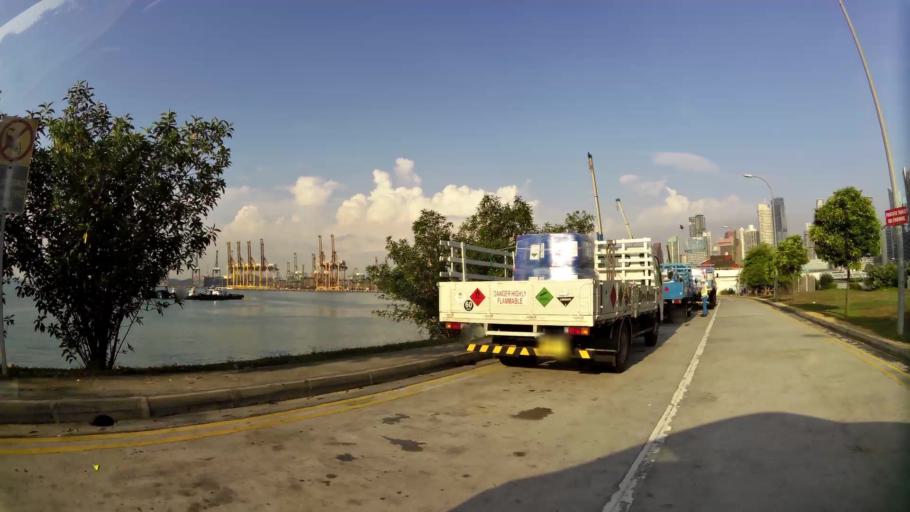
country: SG
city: Singapore
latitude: 1.2697
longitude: 103.8581
